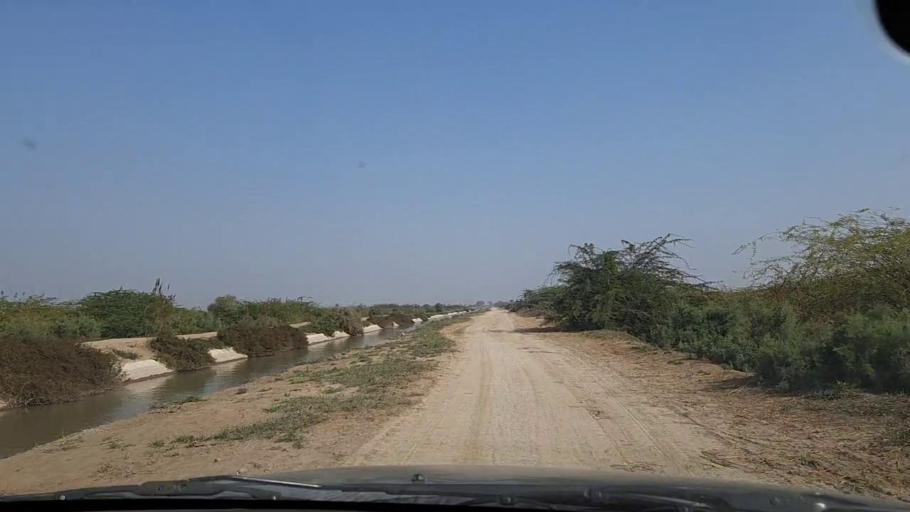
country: PK
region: Sindh
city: Mirpur Sakro
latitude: 24.3419
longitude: 67.7160
